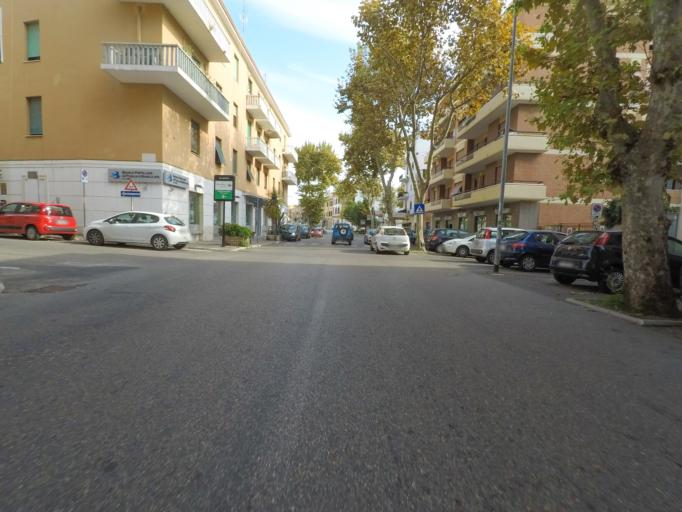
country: IT
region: Latium
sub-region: Citta metropolitana di Roma Capitale
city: Civitavecchia
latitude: 42.0939
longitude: 11.7959
